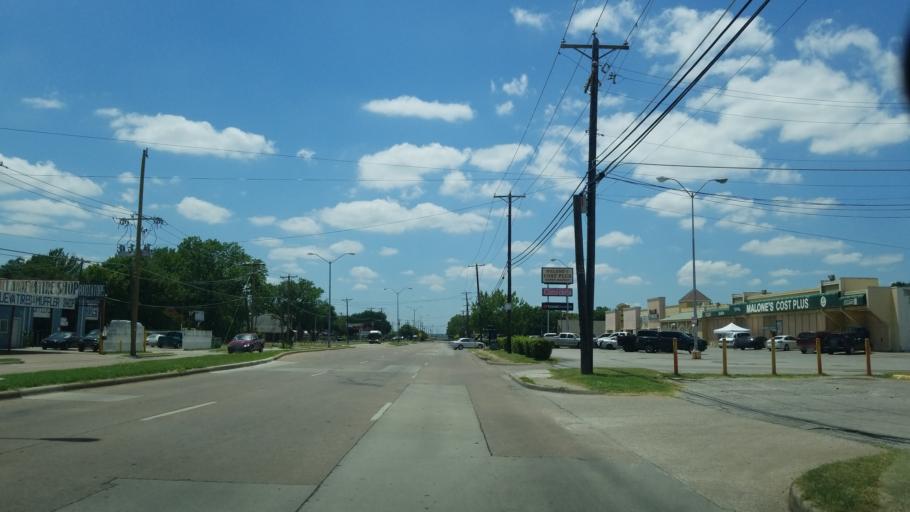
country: US
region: Texas
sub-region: Dallas County
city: Balch Springs
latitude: 32.7344
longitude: -96.7009
